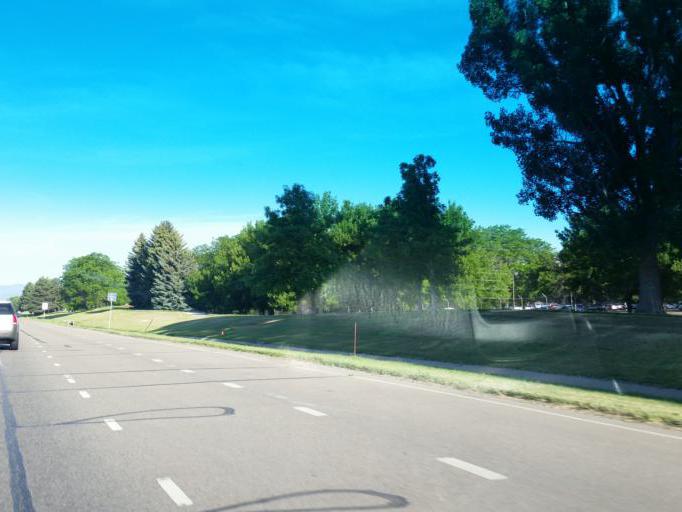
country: US
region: Colorado
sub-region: Larimer County
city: Fort Collins
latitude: 40.5235
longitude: -105.0114
